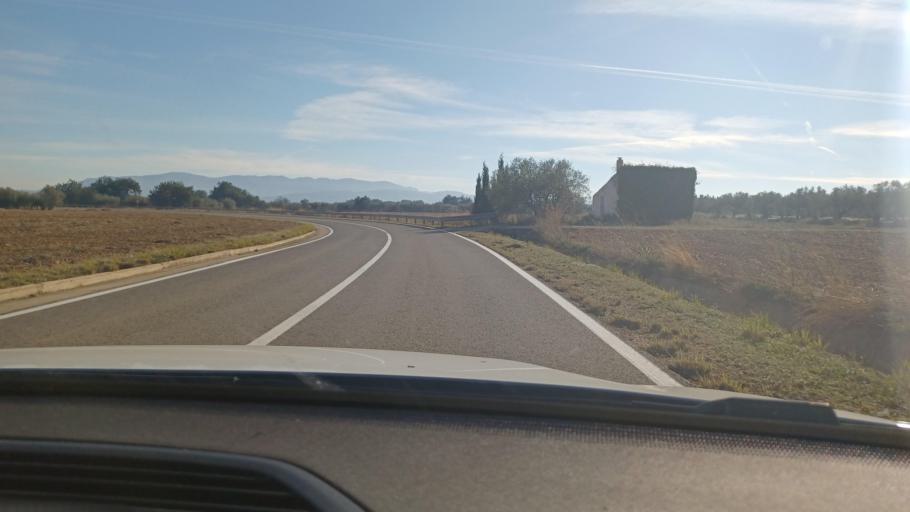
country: ES
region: Catalonia
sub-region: Provincia de Tarragona
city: Santa Barbara
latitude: 40.7204
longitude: 0.4469
